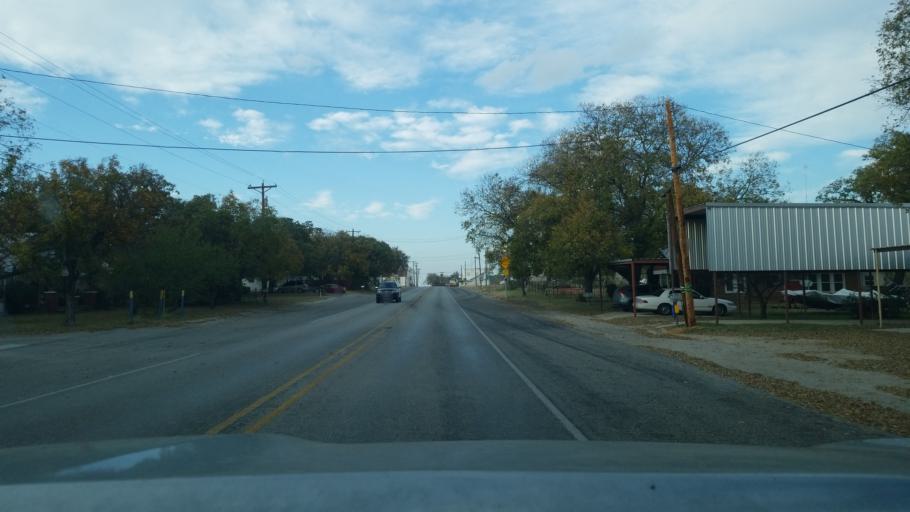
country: US
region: Texas
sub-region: Brown County
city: Lake Brownwood
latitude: 31.9767
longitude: -98.9204
